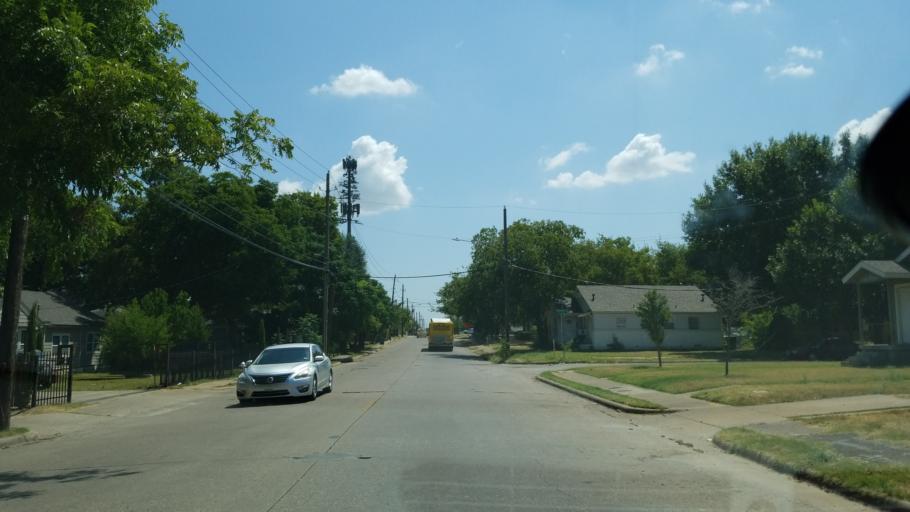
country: US
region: Texas
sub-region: Dallas County
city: Cockrell Hill
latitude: 32.7350
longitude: -96.8861
